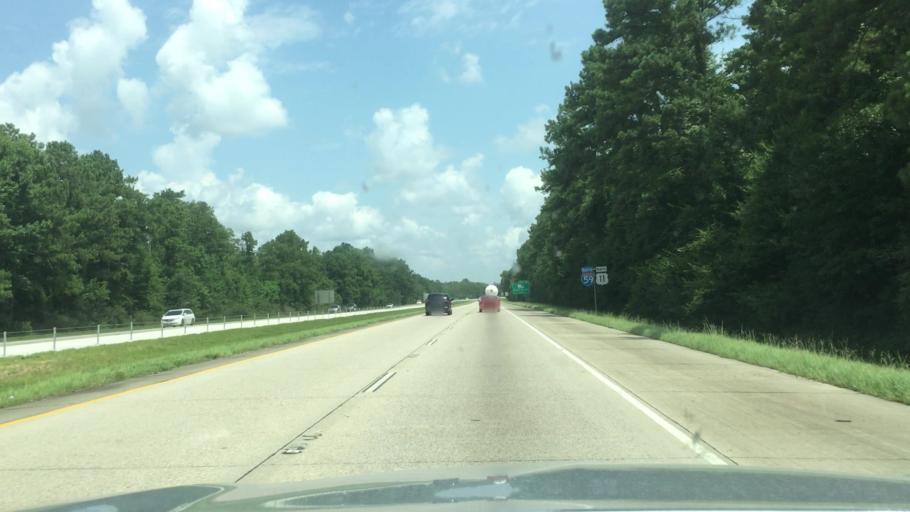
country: US
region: Louisiana
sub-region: Saint Tammany Parish
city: Pearl River
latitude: 30.3589
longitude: -89.7416
